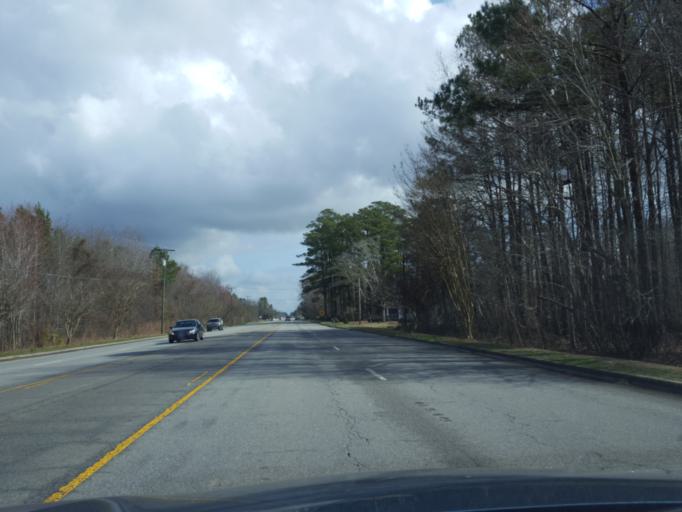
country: US
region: North Carolina
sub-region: Washington County
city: Plymouth
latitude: 35.8696
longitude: -76.7072
